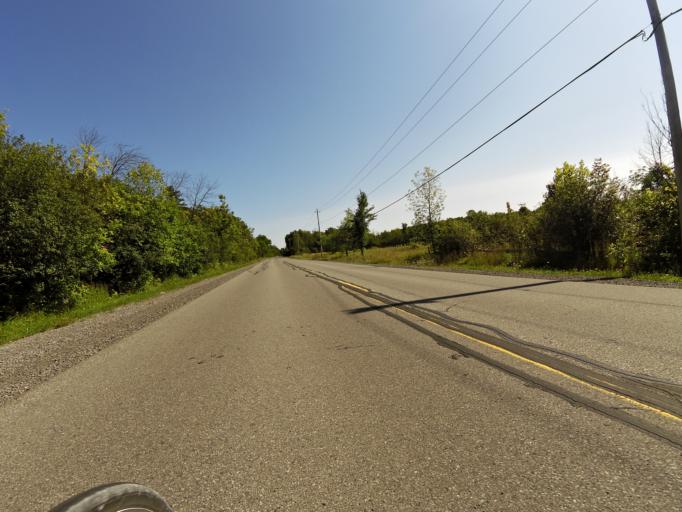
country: CA
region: Ontario
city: Bells Corners
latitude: 45.4178
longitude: -75.9429
